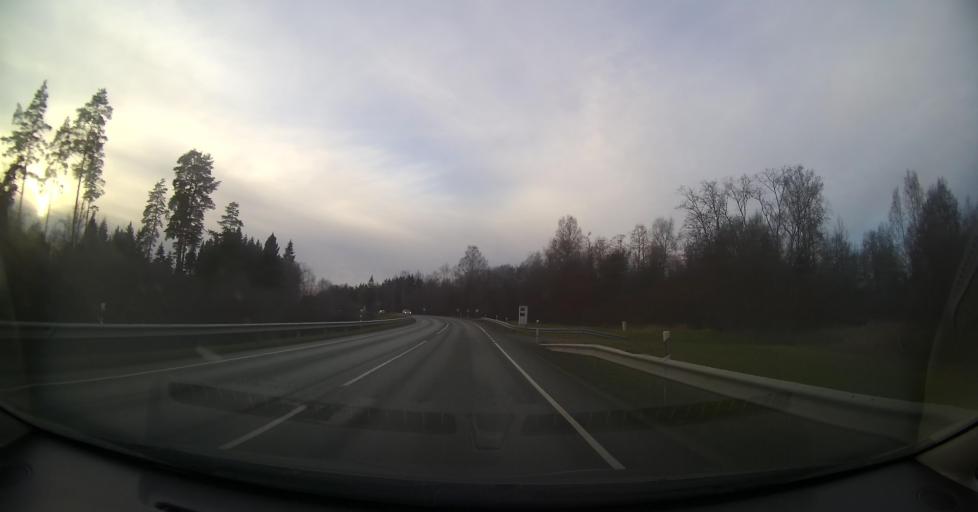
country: EE
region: Ida-Virumaa
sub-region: Toila vald
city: Voka
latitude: 59.3801
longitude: 27.5561
